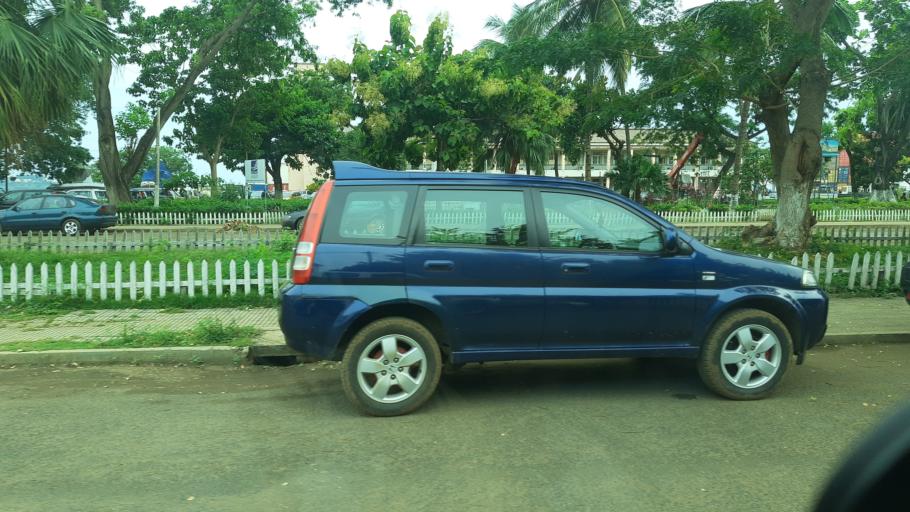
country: ST
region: Sao Tome Island
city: Sao Tome
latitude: 0.3447
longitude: 6.7372
